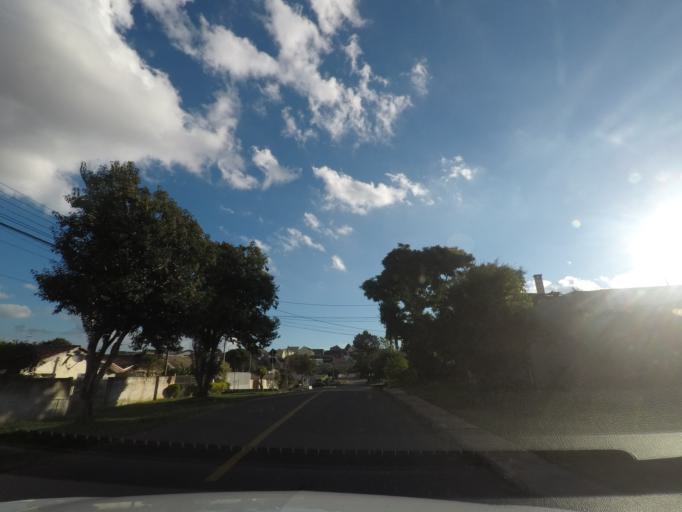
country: BR
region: Parana
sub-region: Sao Jose Dos Pinhais
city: Sao Jose dos Pinhais
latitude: -25.4977
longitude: -49.2618
